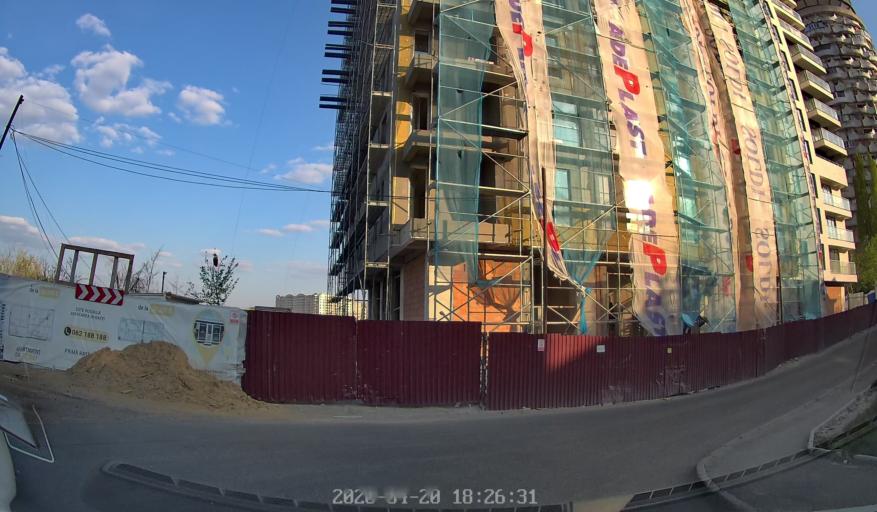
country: MD
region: Chisinau
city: Chisinau
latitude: 46.9918
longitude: 28.8378
